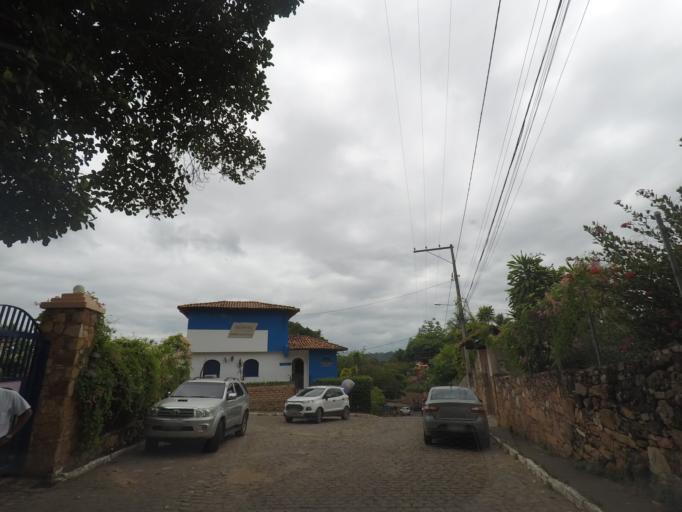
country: BR
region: Bahia
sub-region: Andarai
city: Vera Cruz
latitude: -12.5651
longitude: -41.3938
